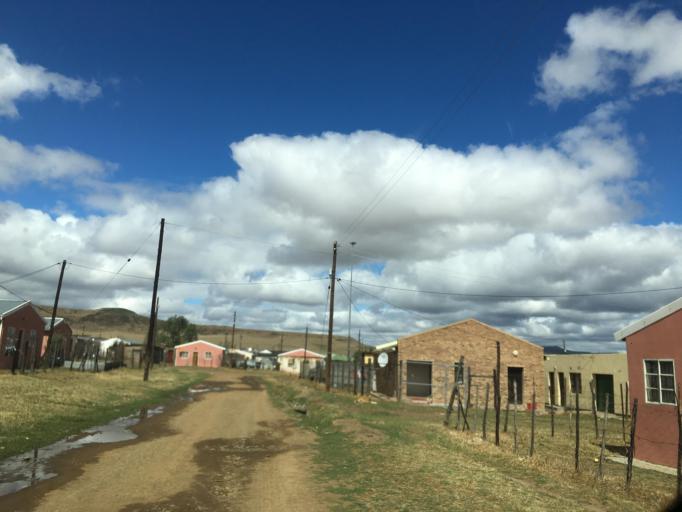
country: ZA
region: Eastern Cape
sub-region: Chris Hani District Municipality
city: Cala
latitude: -31.5343
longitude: 27.7022
